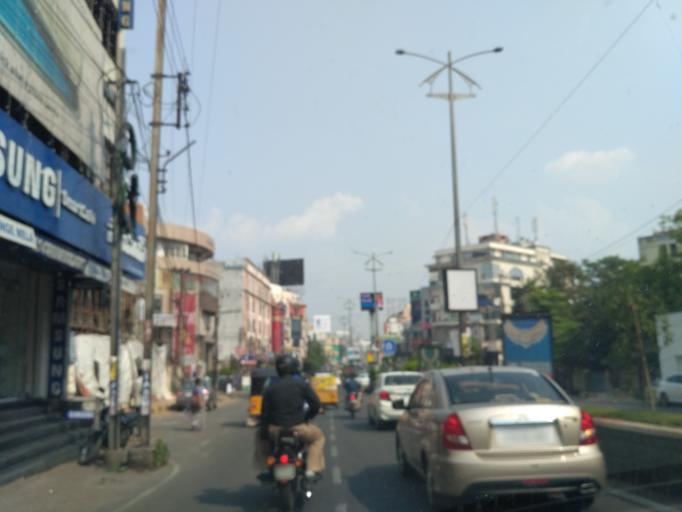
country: IN
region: Telangana
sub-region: Hyderabad
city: Hyderabad
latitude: 17.4057
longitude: 78.4796
